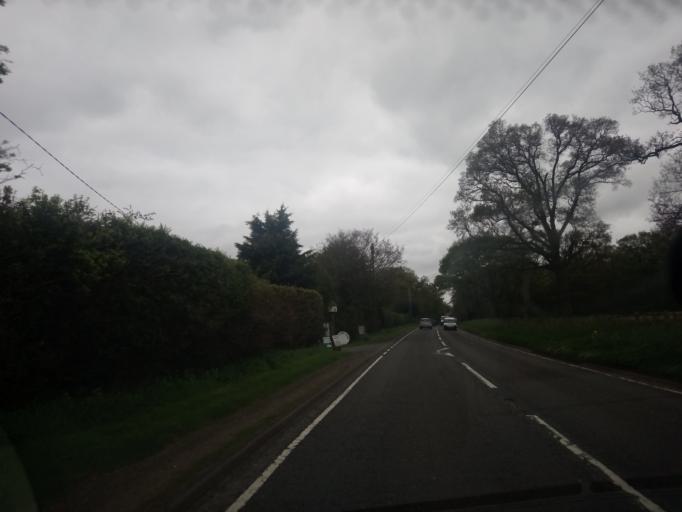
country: GB
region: England
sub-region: Telford and Wrekin
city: Chetwynd
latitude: 52.7952
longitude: -2.4154
